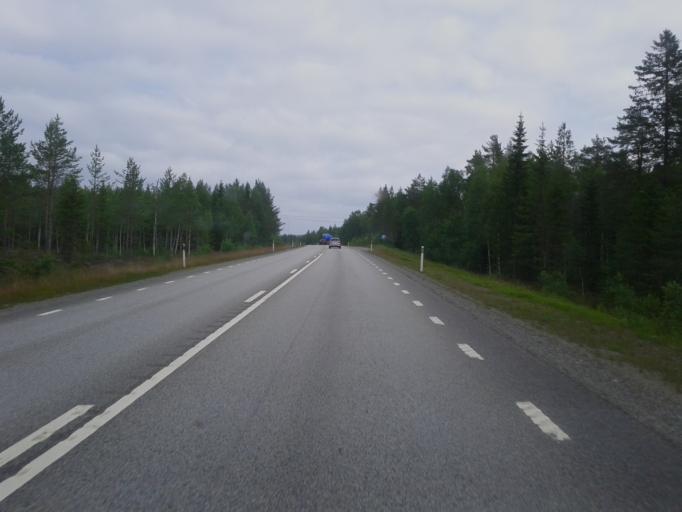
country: SE
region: Vaesterbotten
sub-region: Robertsfors Kommun
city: Robertsfors
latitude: 64.2788
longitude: 21.0617
